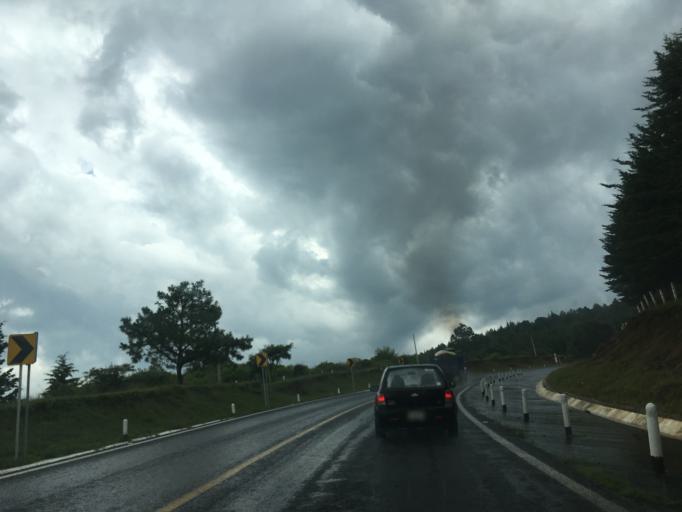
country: MX
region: Michoacan
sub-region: Patzcuaro
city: Santa Ana Chapitiro
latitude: 19.5077
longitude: -101.6959
